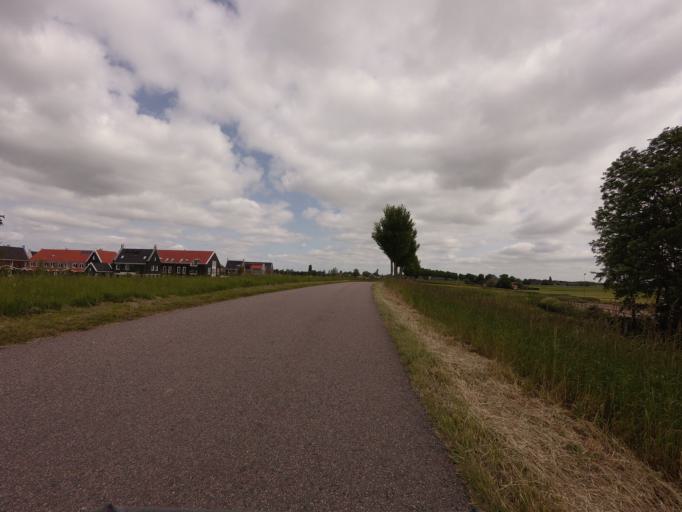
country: NL
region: North Holland
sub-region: Gemeente Beemster
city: Halfweg
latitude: 52.5544
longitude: 4.8519
